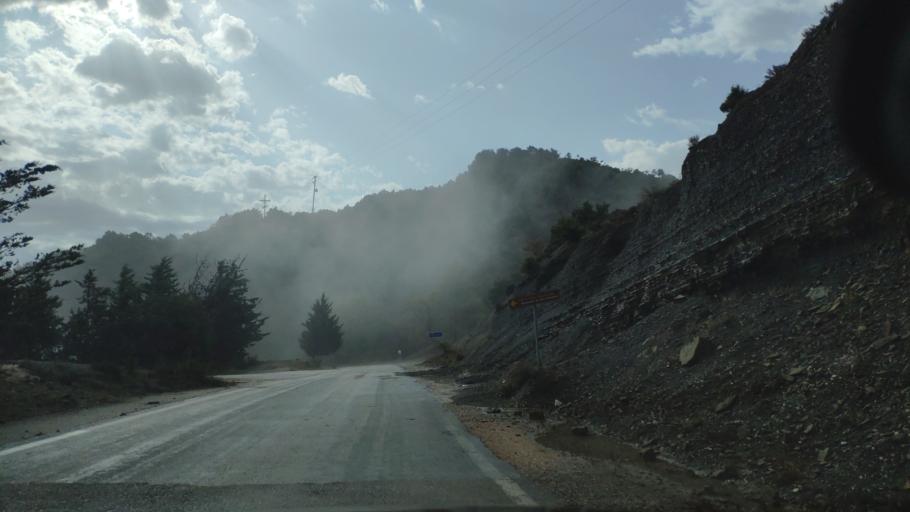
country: GR
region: West Greece
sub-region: Nomos Aitolias kai Akarnanias
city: Sardinia
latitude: 38.8705
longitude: 21.2821
